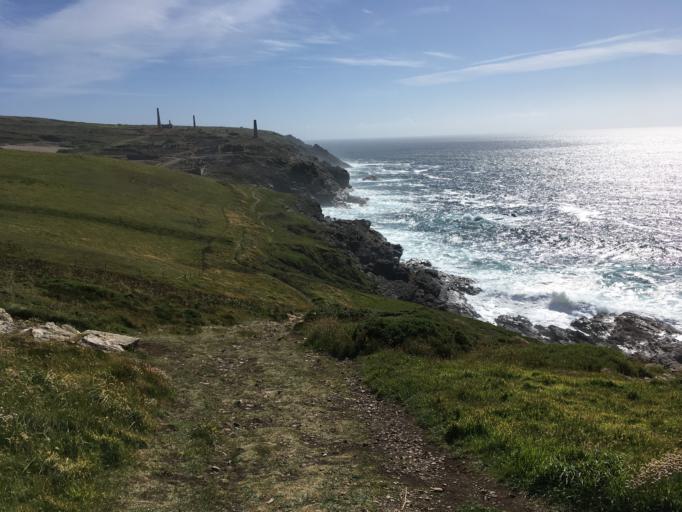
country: GB
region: England
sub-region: Cornwall
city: Saint Just
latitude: 50.1589
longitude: -5.6770
